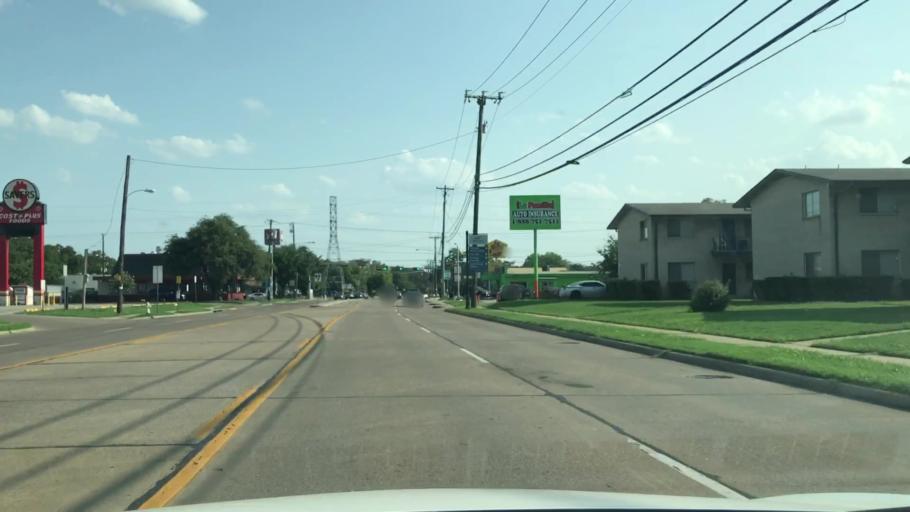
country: US
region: Texas
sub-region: Dallas County
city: Irving
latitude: 32.8195
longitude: -96.9496
